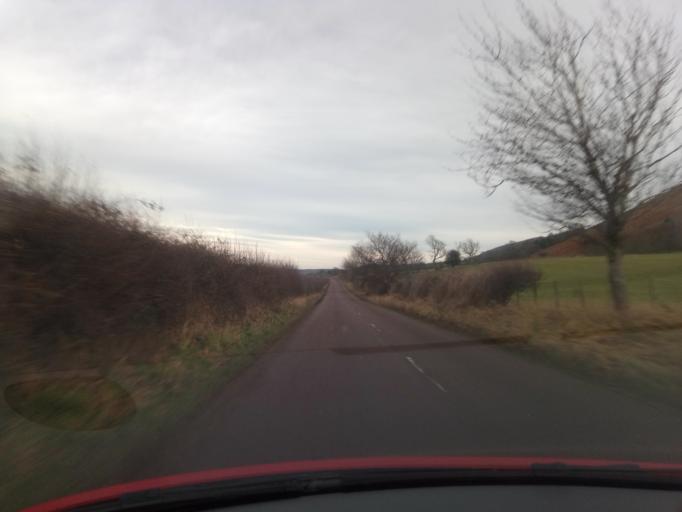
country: GB
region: England
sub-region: Northumberland
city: Kirknewton
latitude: 55.5634
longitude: -2.0861
